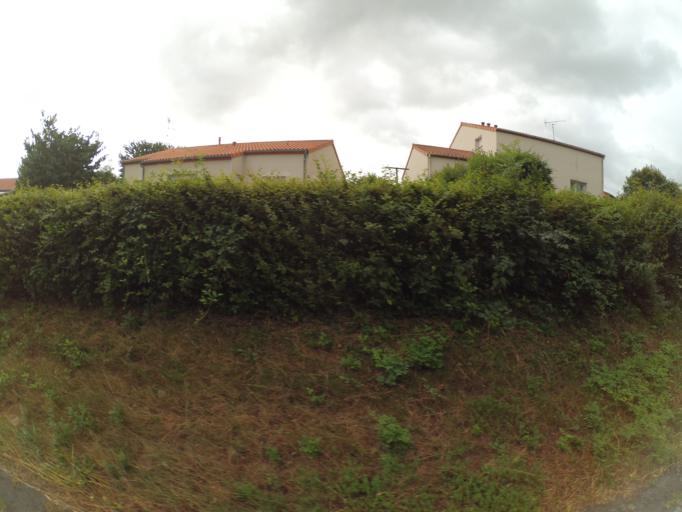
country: FR
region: Pays de la Loire
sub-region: Departement de Maine-et-Loire
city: Montfaucon-Montigne
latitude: 47.0907
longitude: -1.1355
